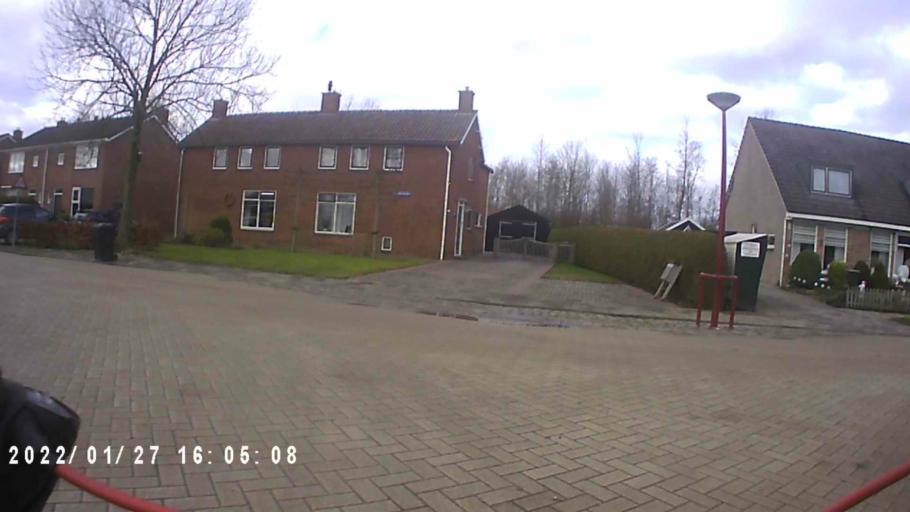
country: NL
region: Friesland
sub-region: Gemeente Dongeradeel
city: Anjum
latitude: 53.3818
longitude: 6.0885
